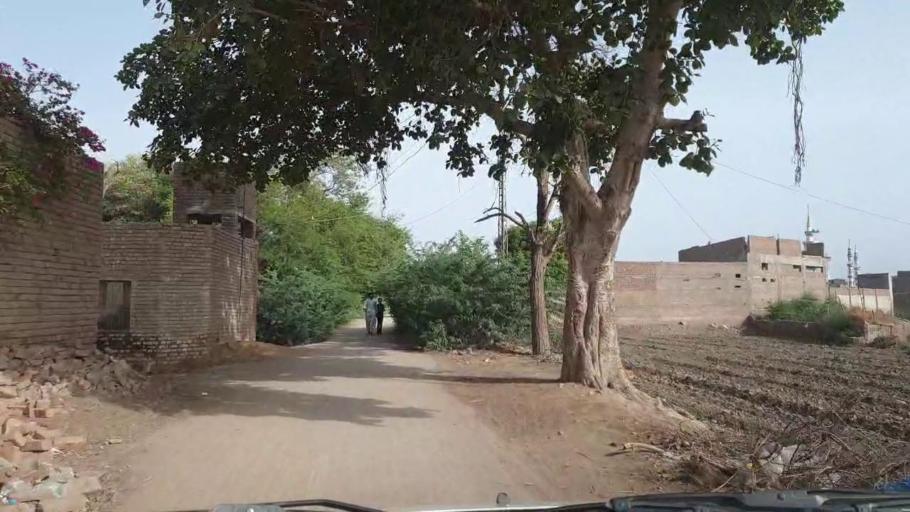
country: PK
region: Sindh
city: Nawabshah
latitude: 26.2303
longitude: 68.4101
